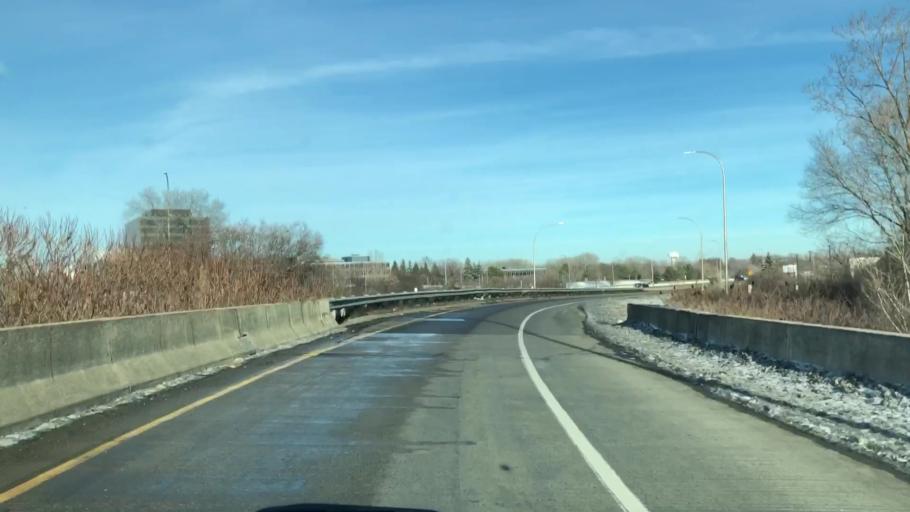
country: US
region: Minnesota
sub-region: Hennepin County
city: Minnetonka Mills
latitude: 44.9716
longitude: -93.4001
